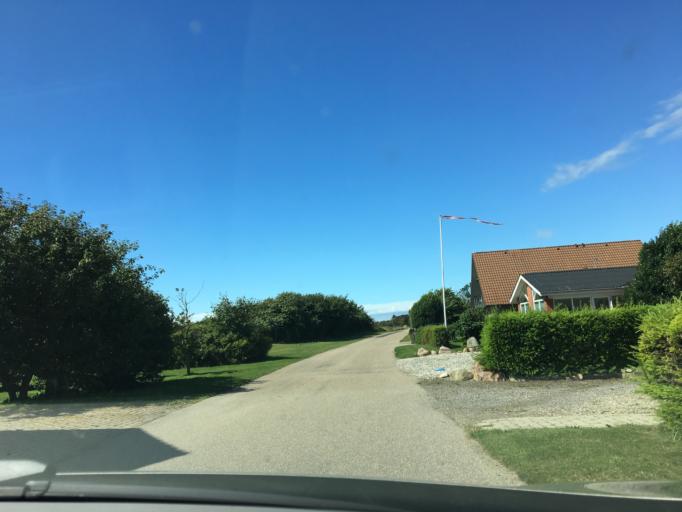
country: DK
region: Central Jutland
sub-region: Ringkobing-Skjern Kommune
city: Ringkobing
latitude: 56.0957
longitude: 8.2233
